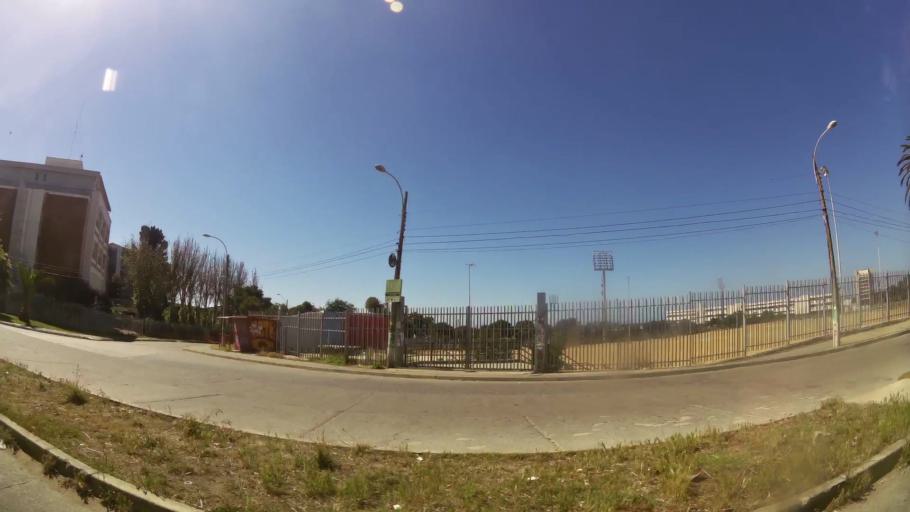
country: CL
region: Valparaiso
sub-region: Provincia de Valparaiso
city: Valparaiso
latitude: -33.0248
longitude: -71.6400
